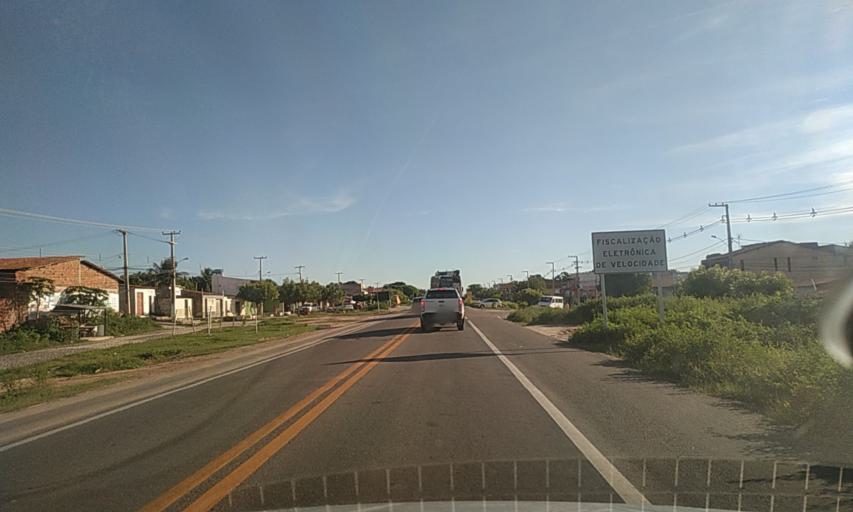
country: BR
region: Rio Grande do Norte
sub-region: Mossoro
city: Mossoro
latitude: -5.1962
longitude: -37.3159
